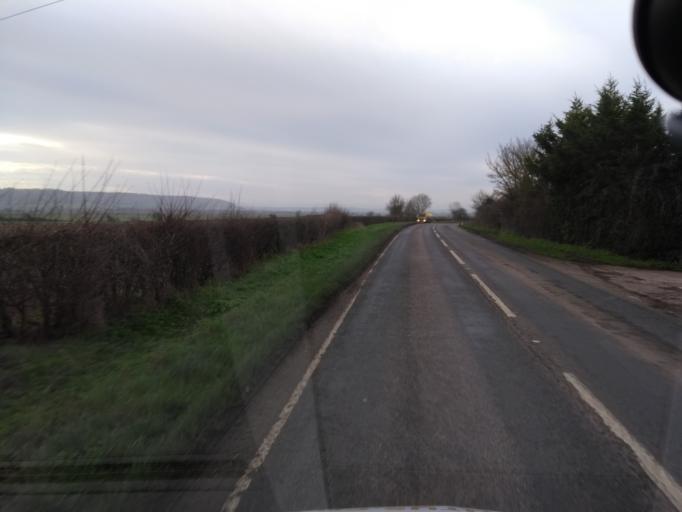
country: GB
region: England
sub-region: Somerset
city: Westonzoyland
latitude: 51.1112
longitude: -2.8537
